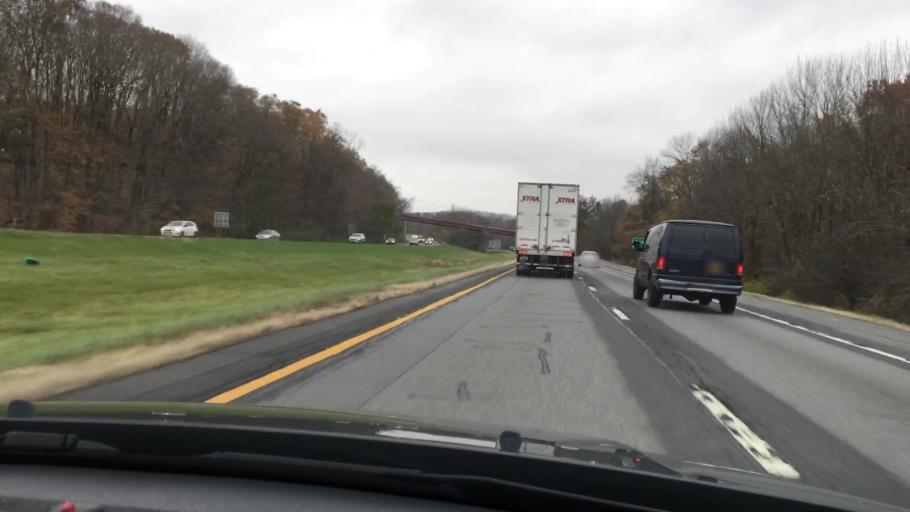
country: US
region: New York
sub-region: Putnam County
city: Lake Carmel
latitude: 41.4945
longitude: -73.6661
